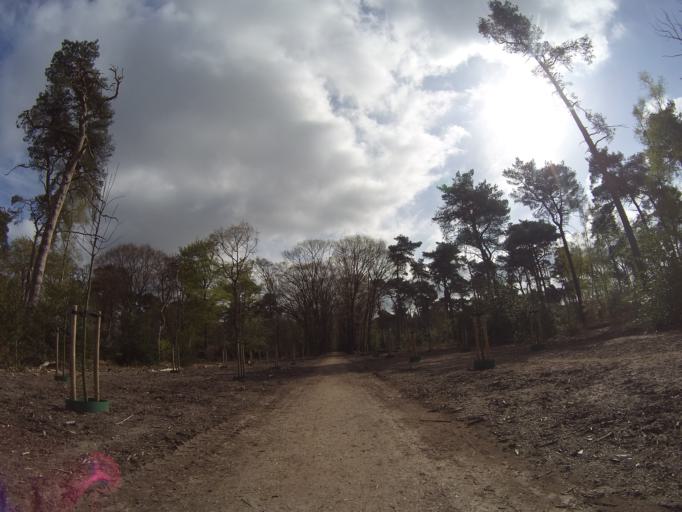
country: NL
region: Utrecht
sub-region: Gemeente Amersfoort
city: Amersfoort
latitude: 52.1332
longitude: 5.3790
